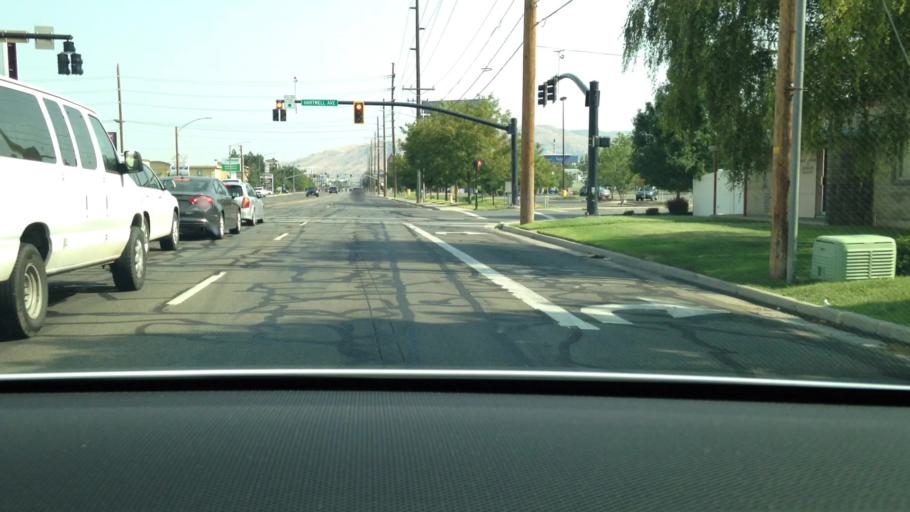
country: US
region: Utah
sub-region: Salt Lake County
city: South Salt Lake
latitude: 40.7274
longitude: -111.8996
